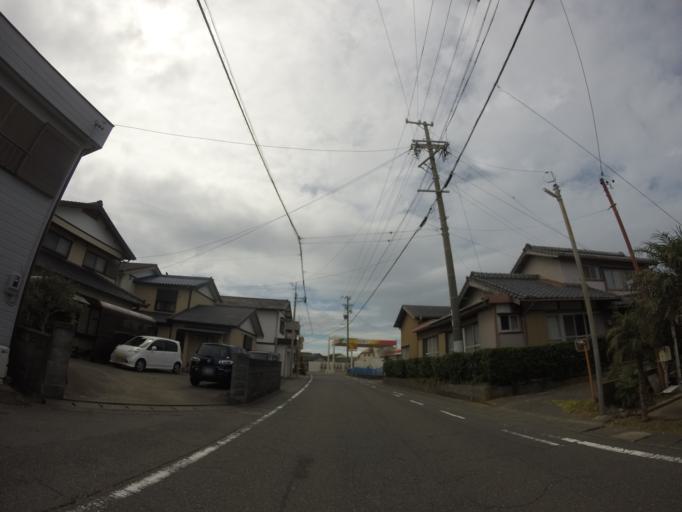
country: JP
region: Shizuoka
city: Oyama
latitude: 34.6073
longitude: 138.2121
